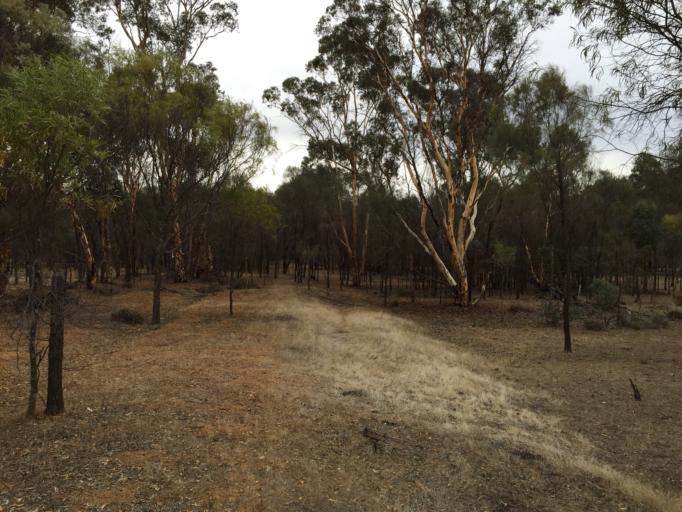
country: AU
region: Western Australia
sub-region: Narrogin
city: Narrogin
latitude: -32.8218
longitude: 116.8892
